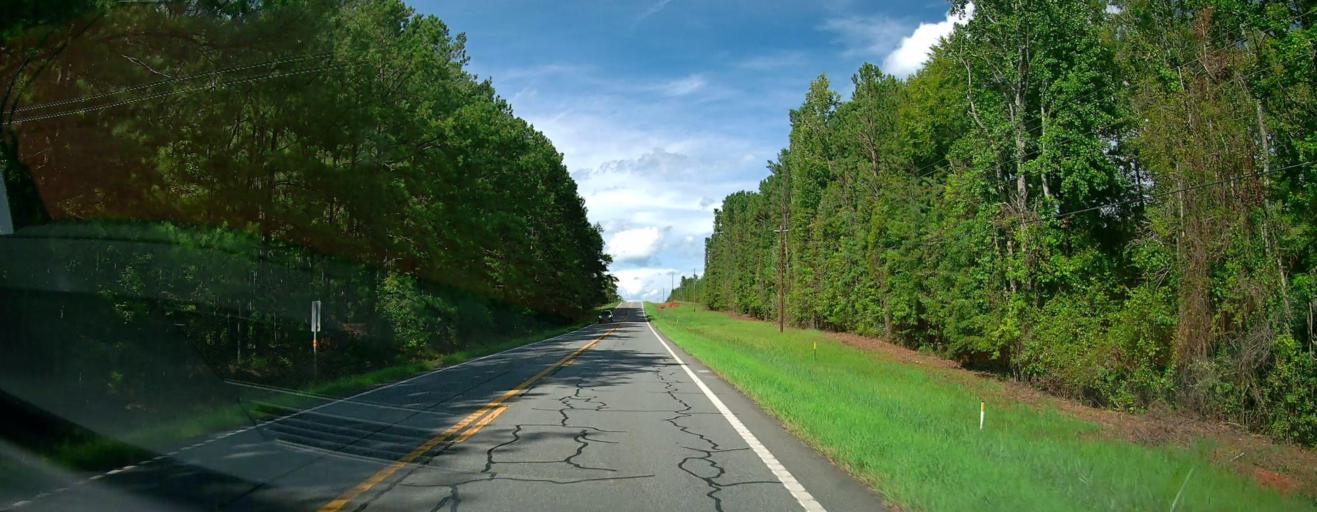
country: US
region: Georgia
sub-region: Talbot County
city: Talbotton
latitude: 32.7188
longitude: -84.5565
